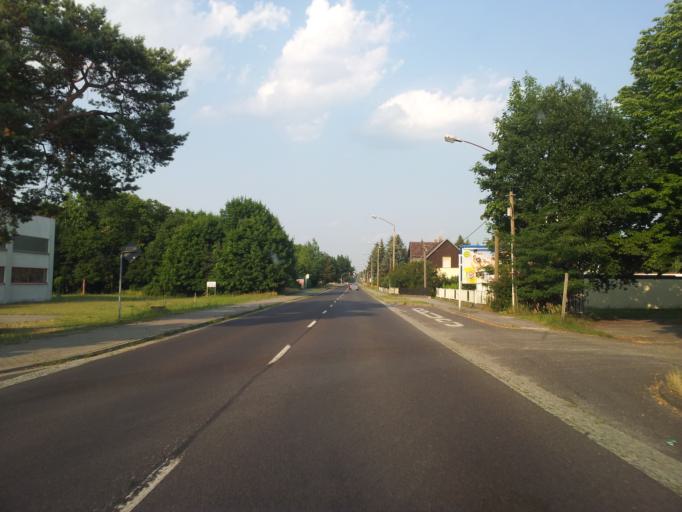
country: DE
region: Saxony
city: Hoyerswerda
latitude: 51.4204
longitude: 14.1898
